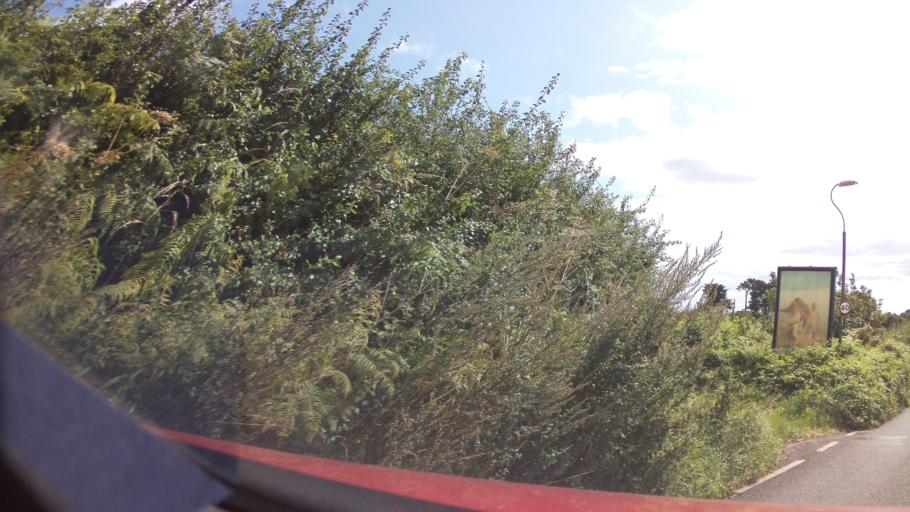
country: GB
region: England
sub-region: Devon
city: Teignmouth
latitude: 50.5119
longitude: -3.5187
